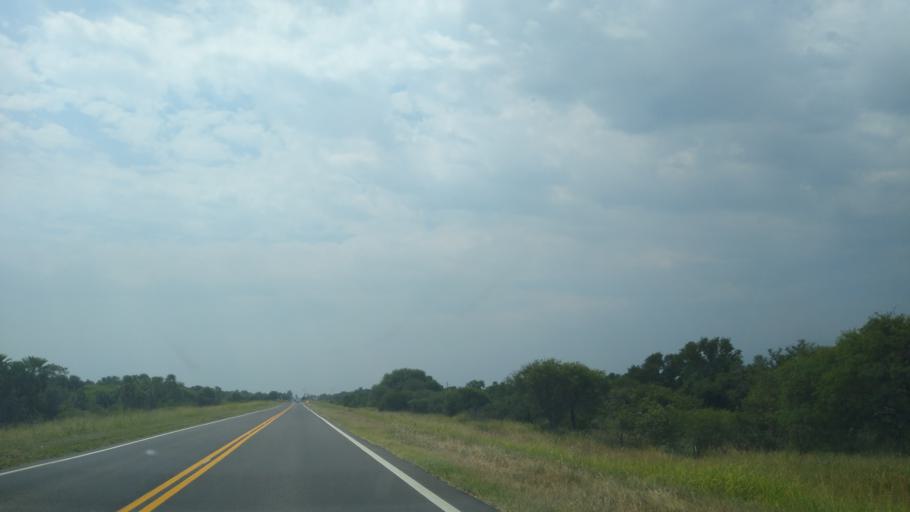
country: AR
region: Chaco
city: Margarita Belen
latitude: -27.1257
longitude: -58.9739
